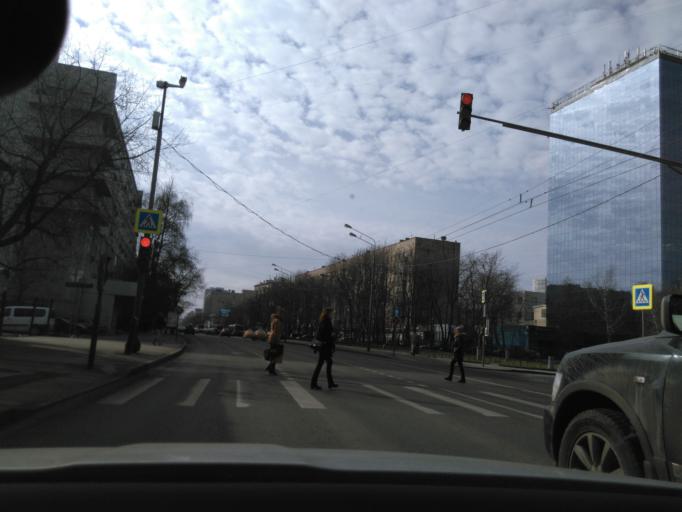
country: RU
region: Moscow
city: Zamoskvorech'ye
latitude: 55.7240
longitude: 37.6225
